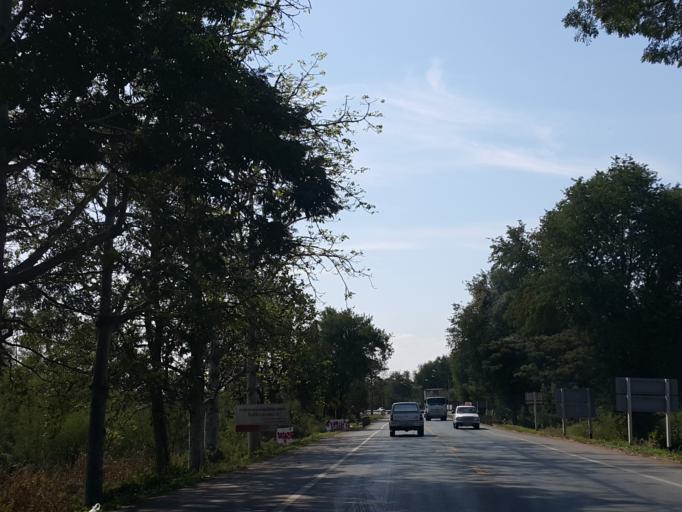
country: TH
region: Sukhothai
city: Sawankhalok
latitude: 17.2746
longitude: 99.8420
